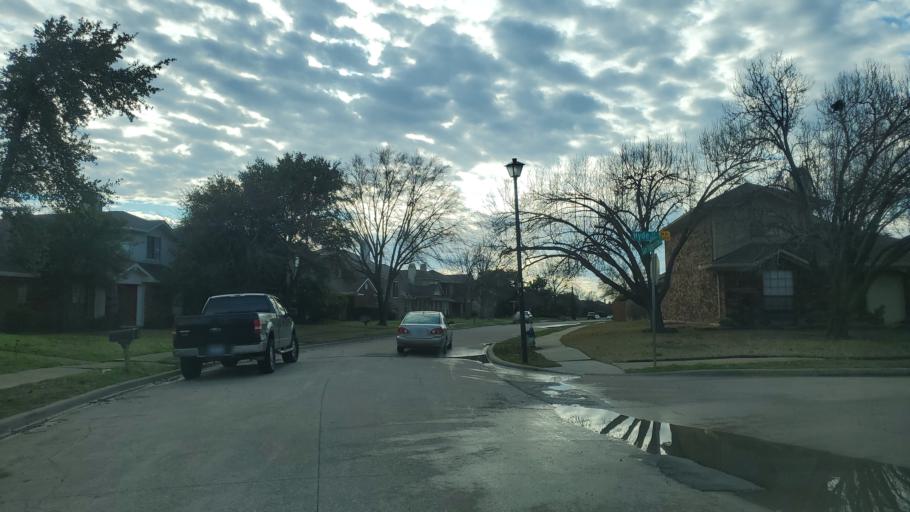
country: US
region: Texas
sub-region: Dallas County
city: Carrollton
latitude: 32.9976
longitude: -96.8970
